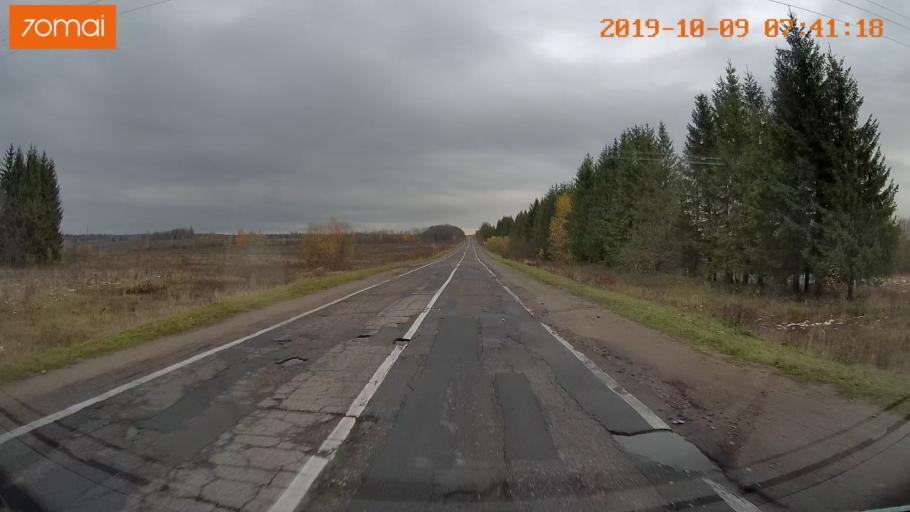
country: RU
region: Jaroslavl
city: Kukoboy
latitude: 58.6382
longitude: 39.7048
